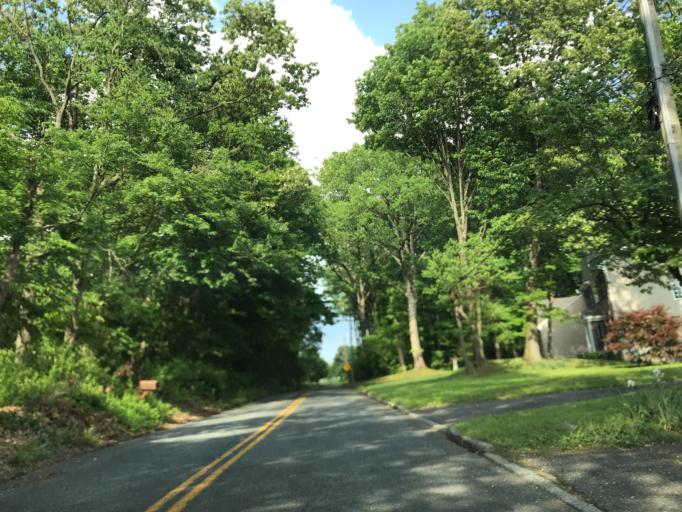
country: US
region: Maryland
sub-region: Harford County
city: Bel Air North
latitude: 39.5733
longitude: -76.3902
